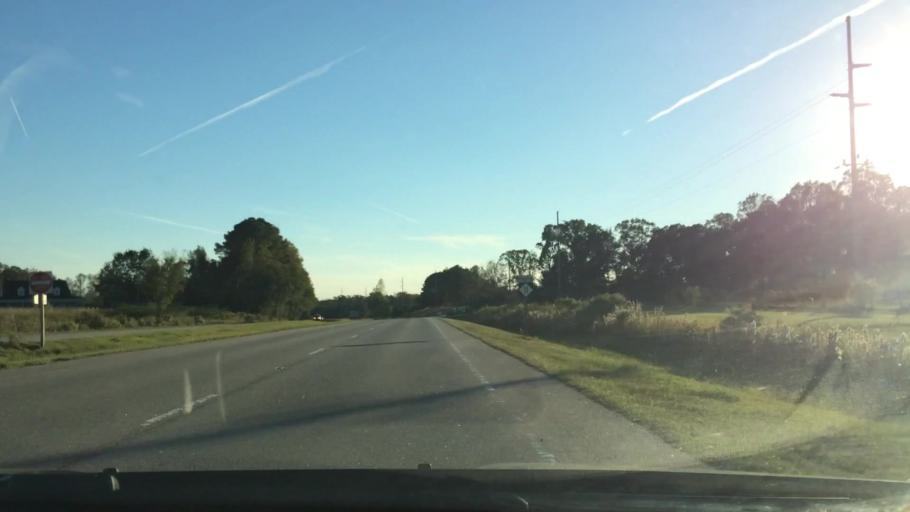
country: US
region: North Carolina
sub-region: Pitt County
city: Grifton
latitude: 35.3964
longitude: -77.4428
